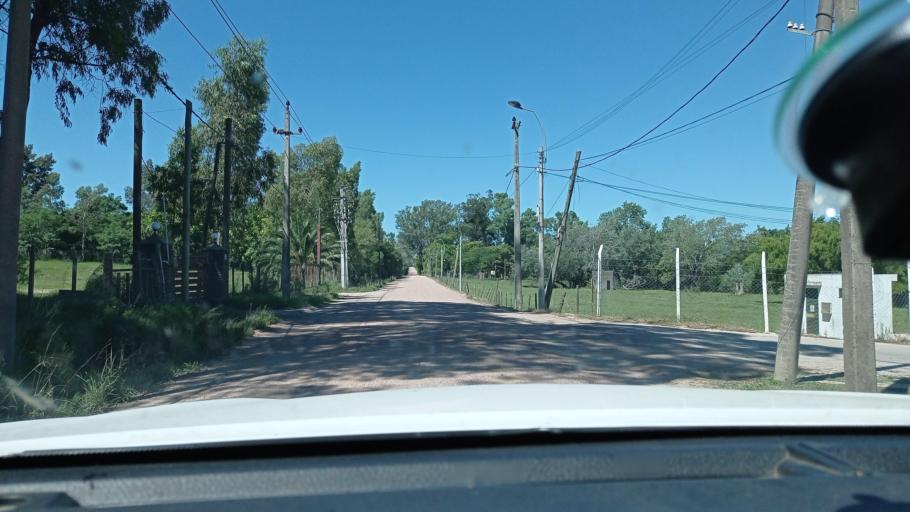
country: UY
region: Canelones
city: La Paz
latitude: -34.7599
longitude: -56.1732
